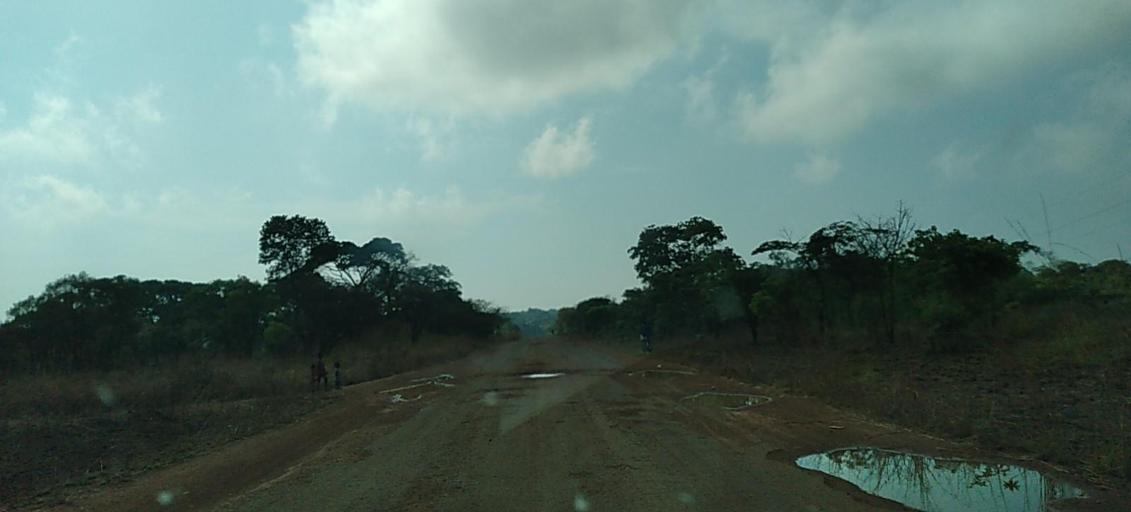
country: ZM
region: North-Western
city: Mwinilunga
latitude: -11.7672
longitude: 25.0035
